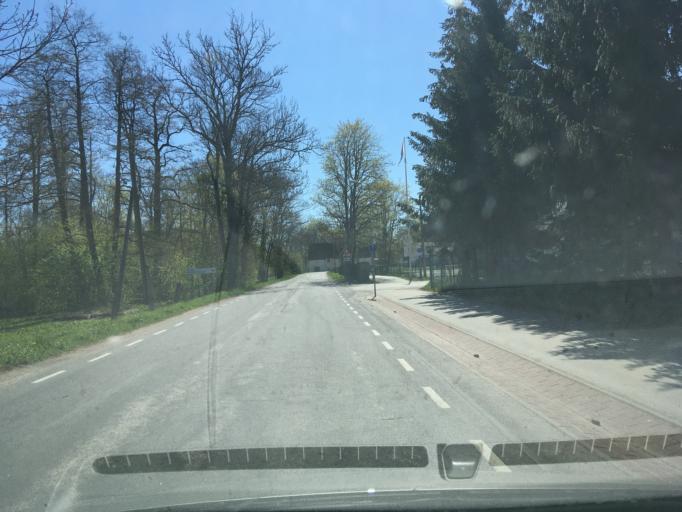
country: EE
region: Harju
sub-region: Raasiku vald
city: Arukula
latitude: 59.3599
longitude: 25.0825
